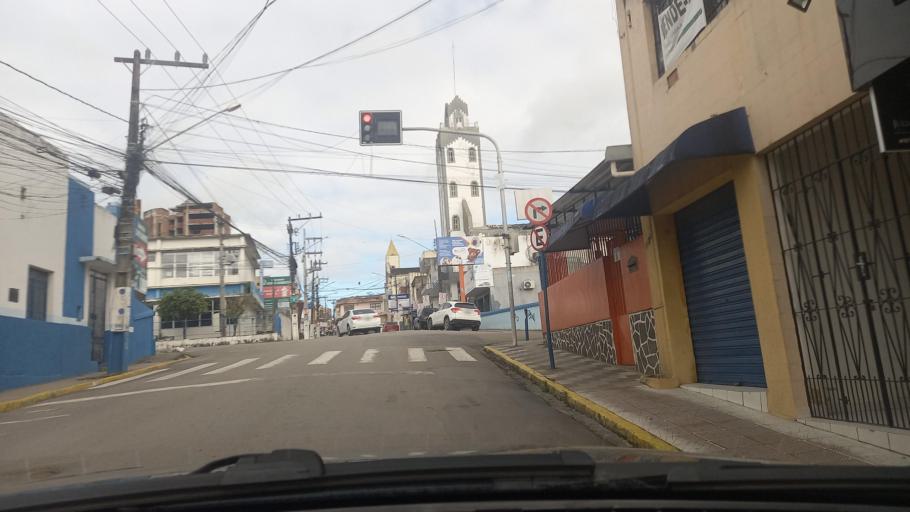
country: BR
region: Pernambuco
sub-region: Vitoria De Santo Antao
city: Vitoria de Santo Antao
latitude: -8.1191
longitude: -35.2977
